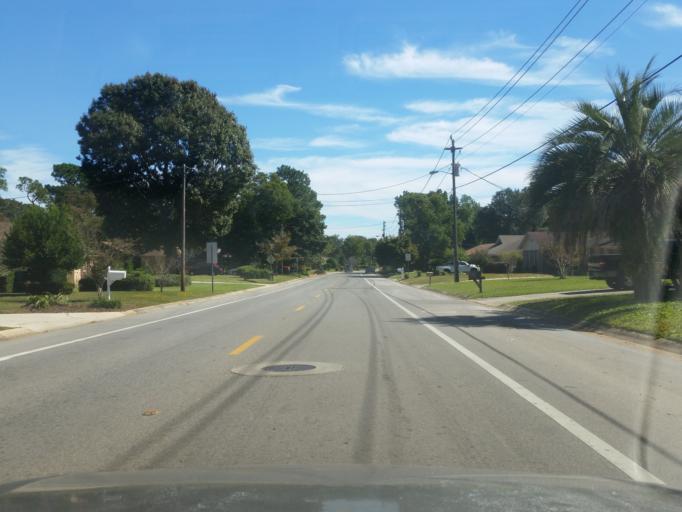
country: US
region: Florida
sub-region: Escambia County
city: East Pensacola Heights
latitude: 30.4622
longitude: -87.1740
